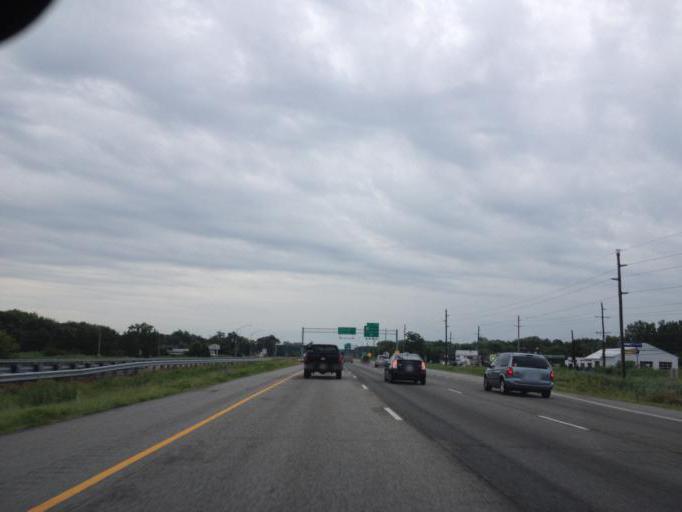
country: US
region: Maryland
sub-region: Queen Anne's County
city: Grasonville
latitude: 38.9655
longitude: -76.2250
